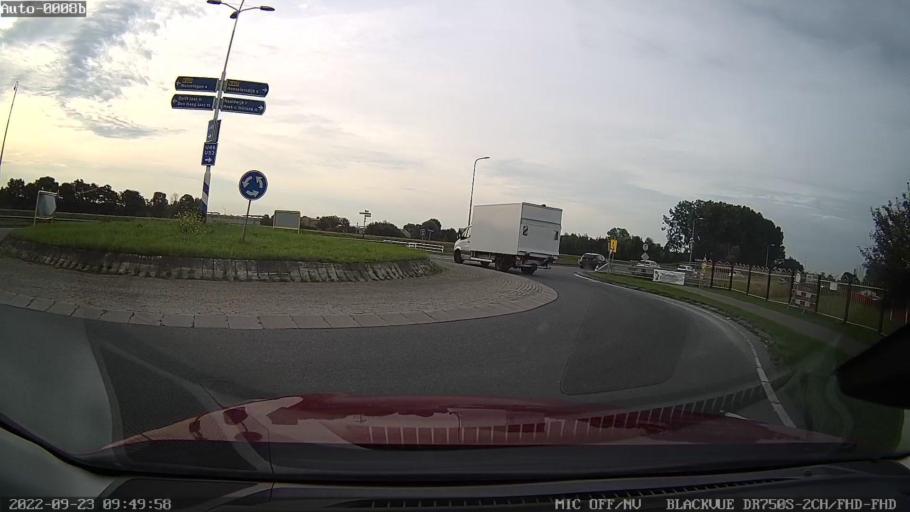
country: NL
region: South Holland
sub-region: Gemeente Westland
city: Kwintsheul
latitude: 51.9957
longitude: 4.2596
